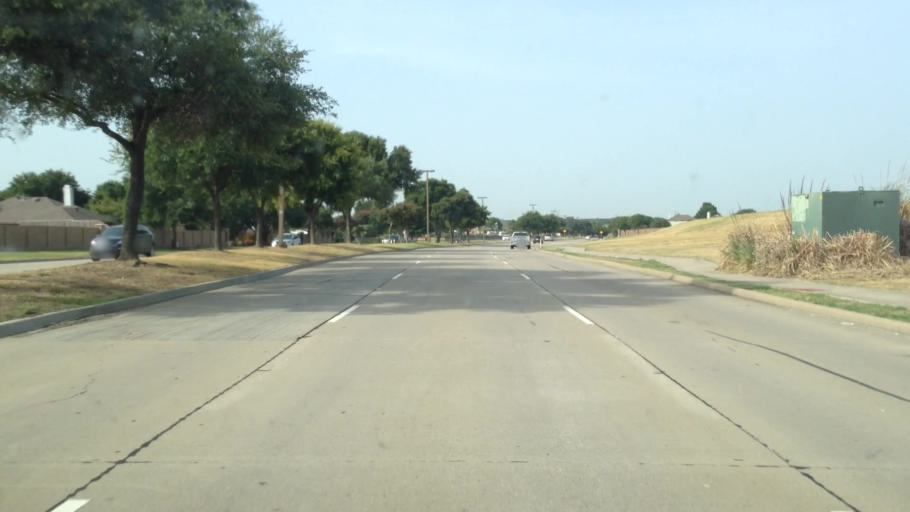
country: US
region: Texas
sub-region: Denton County
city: Lewisville
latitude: 33.0199
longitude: -96.9428
